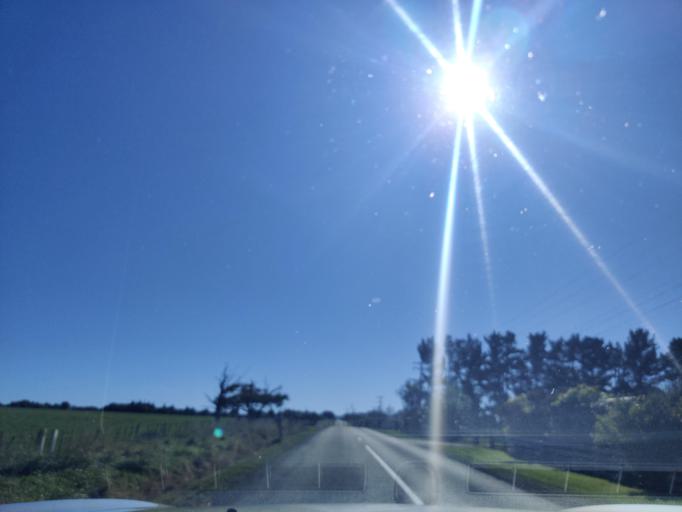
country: NZ
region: Manawatu-Wanganui
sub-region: Palmerston North City
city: Palmerston North
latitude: -40.2882
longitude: 175.6969
